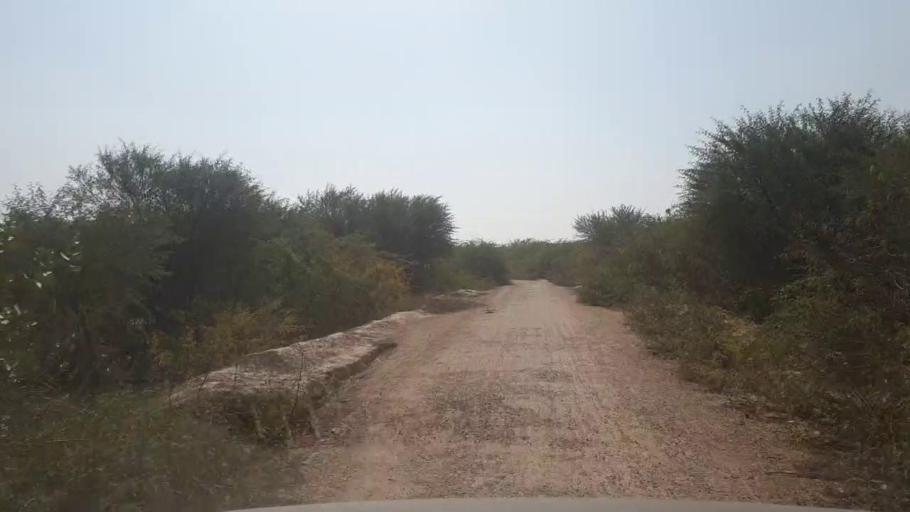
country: PK
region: Sindh
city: Chambar
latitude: 25.2261
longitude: 68.8205
